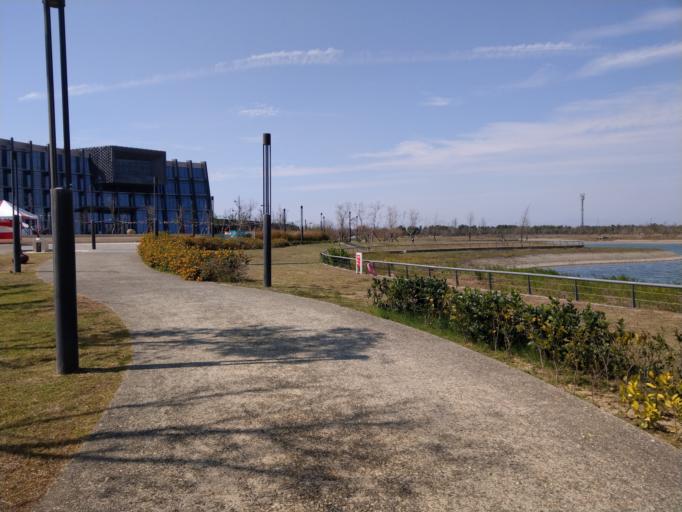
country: TW
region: Taiwan
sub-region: Chiayi
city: Taibao
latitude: 23.4742
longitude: 120.2938
